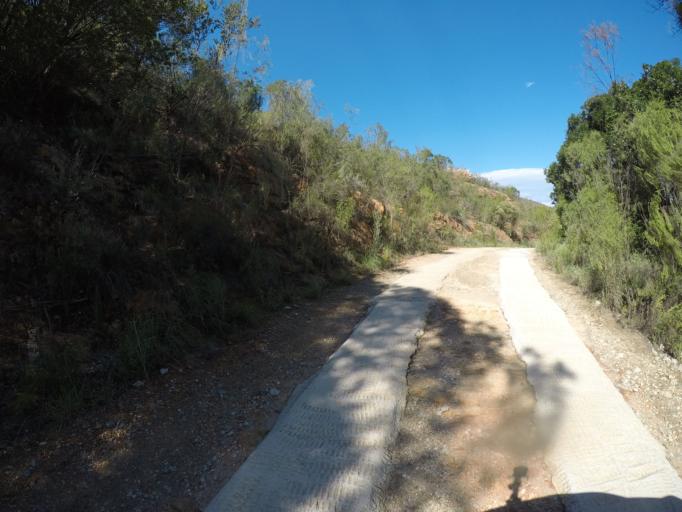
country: ZA
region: Eastern Cape
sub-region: Cacadu District Municipality
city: Kareedouw
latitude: -33.6429
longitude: 24.4623
